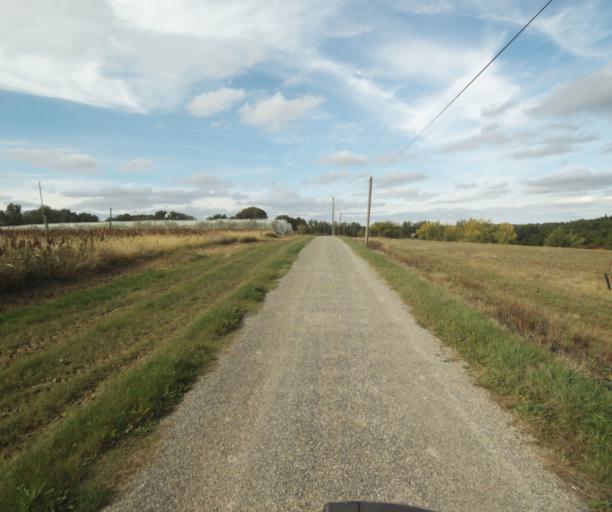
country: FR
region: Midi-Pyrenees
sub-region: Departement du Tarn-et-Garonne
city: Saint-Porquier
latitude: 43.9487
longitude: 1.1329
